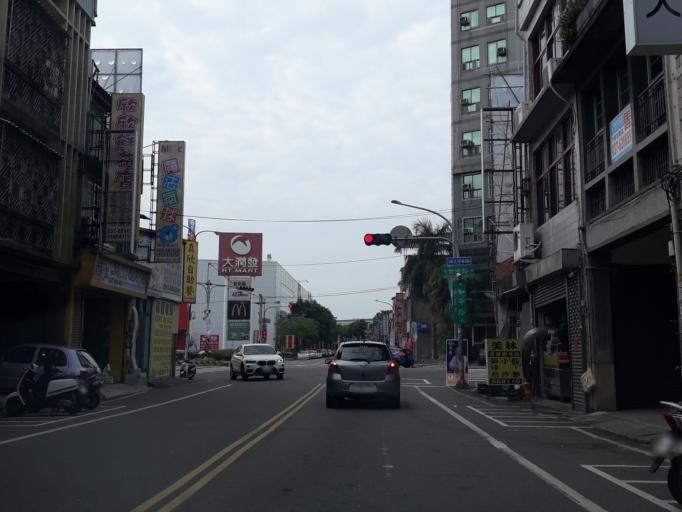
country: TW
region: Taiwan
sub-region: Hsinchu
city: Hsinchu
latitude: 24.6862
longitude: 120.9058
